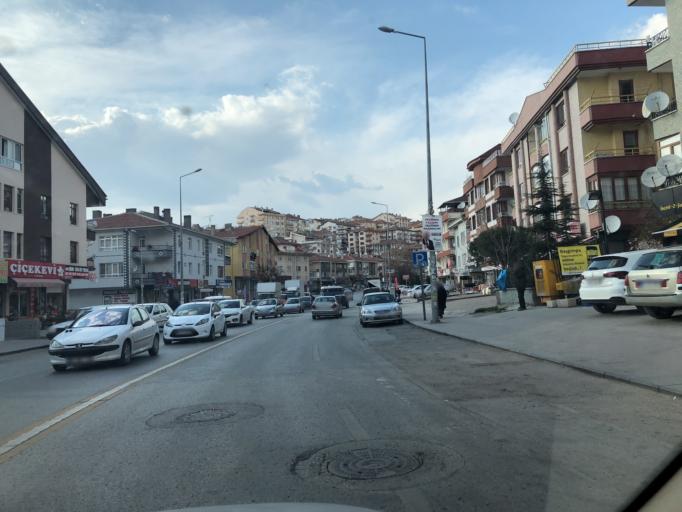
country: TR
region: Ankara
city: Ankara
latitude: 39.9847
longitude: 32.8509
